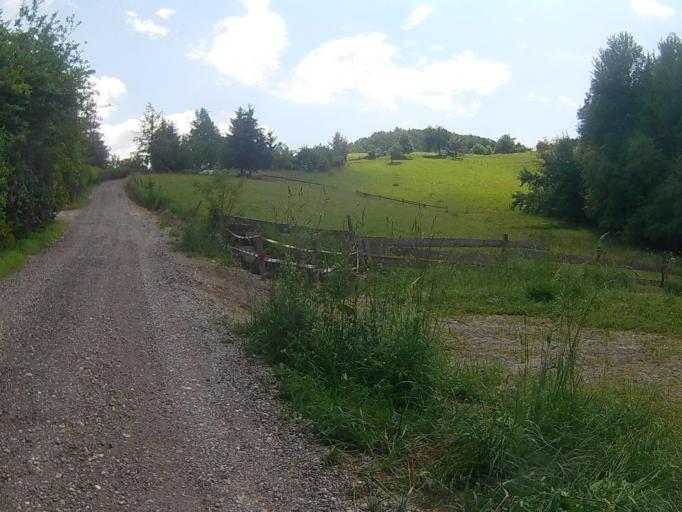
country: SI
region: Kungota
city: Zgornja Kungota
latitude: 46.6156
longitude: 15.5944
